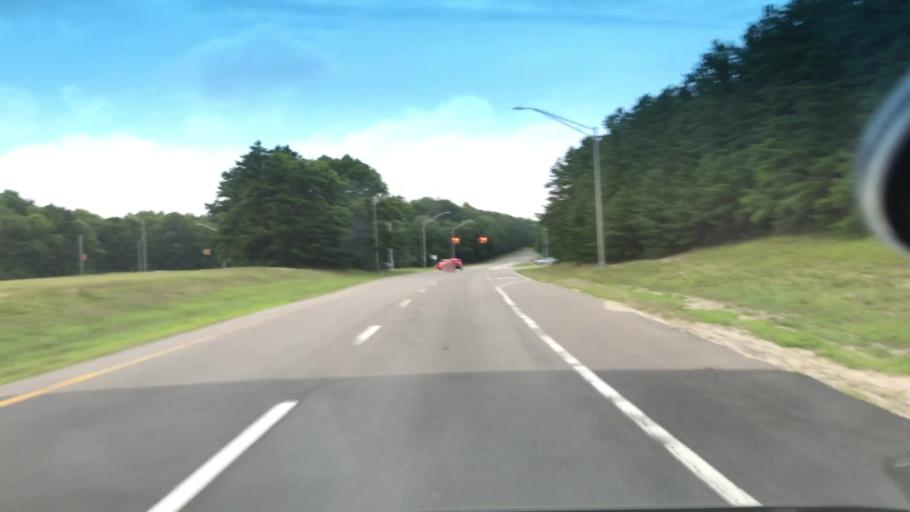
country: US
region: New York
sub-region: Suffolk County
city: Ridge
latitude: 40.8639
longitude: -72.9013
